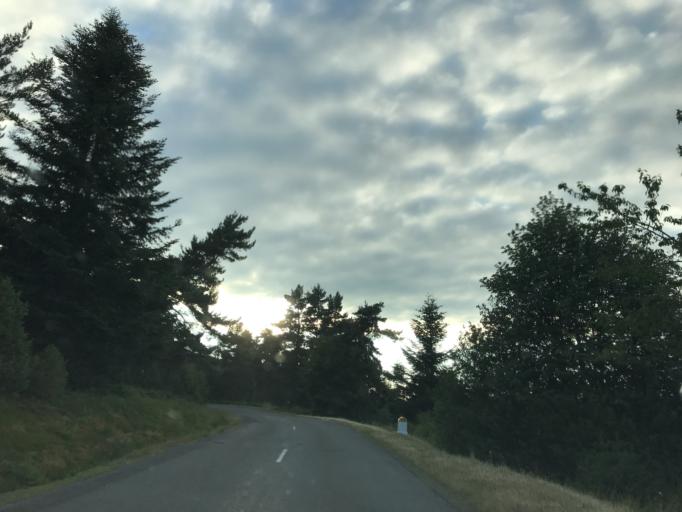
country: FR
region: Rhone-Alpes
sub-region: Departement de la Loire
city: Noiretable
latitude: 45.7636
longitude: 3.8307
